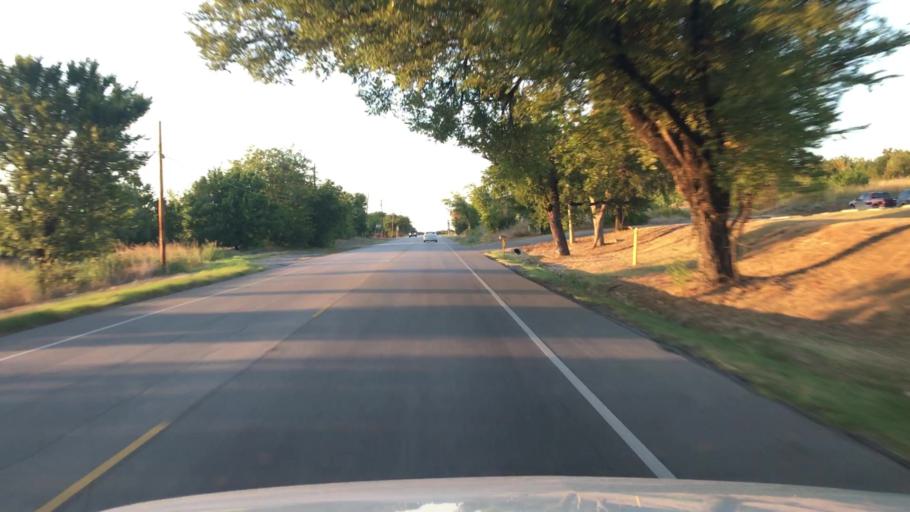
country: US
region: Texas
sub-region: Hamilton County
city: Hico
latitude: 31.9880
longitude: -98.0270
